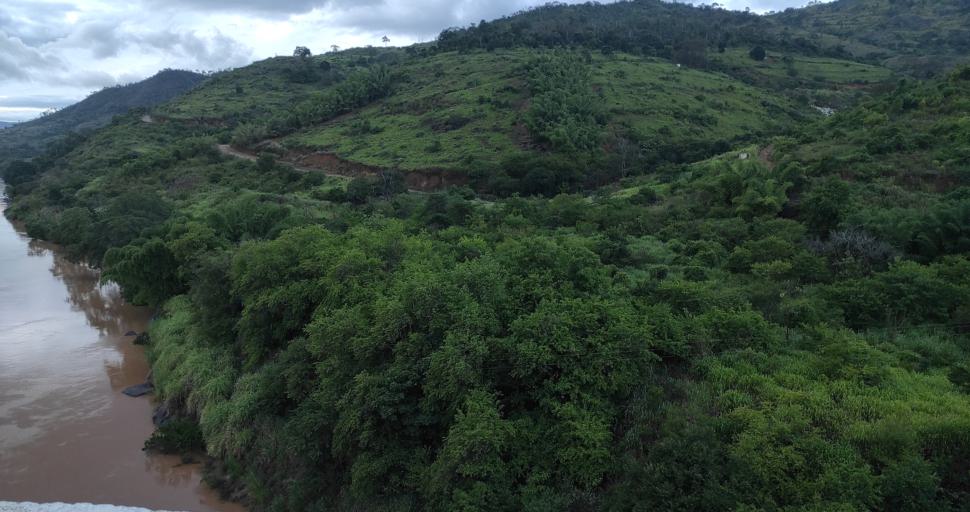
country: BR
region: Espirito Santo
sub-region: Baixo Guandu
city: Baixo Guandu
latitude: -19.5104
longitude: -40.8572
